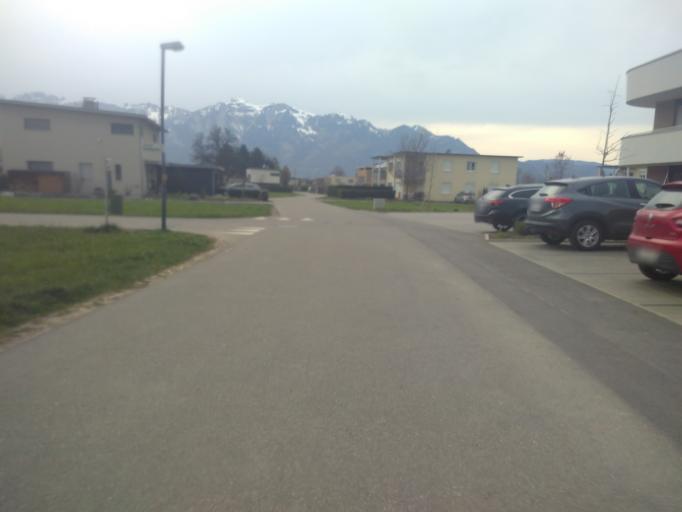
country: AT
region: Vorarlberg
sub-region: Politischer Bezirk Feldkirch
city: Feldkirch
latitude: 47.2634
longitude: 9.6094
